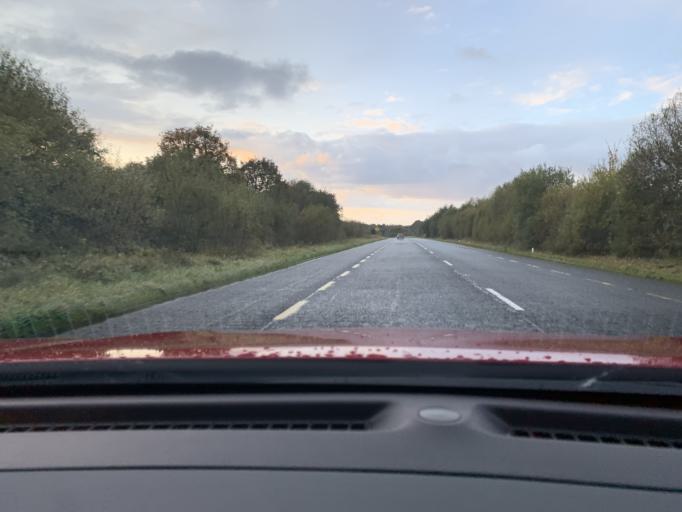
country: IE
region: Connaught
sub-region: County Leitrim
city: Carrick-on-Shannon
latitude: 53.9548
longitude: -8.1576
